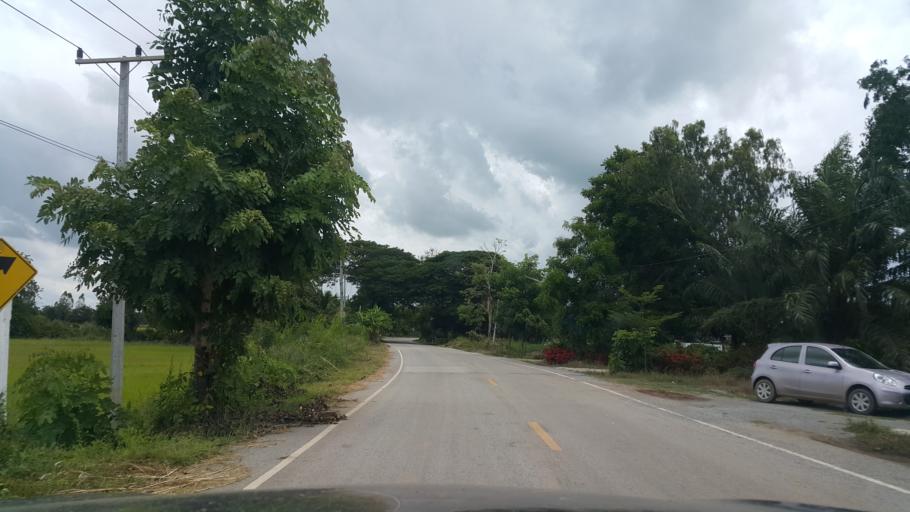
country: TH
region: Sukhothai
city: Kong Krailat
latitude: 16.9293
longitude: 99.9140
